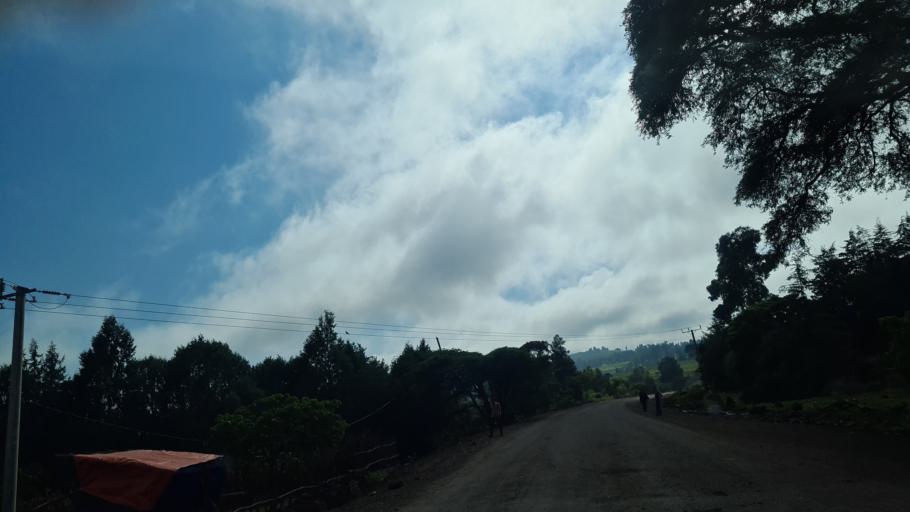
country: ET
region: Oromiya
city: Huruta
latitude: 8.1305
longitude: 39.3825
